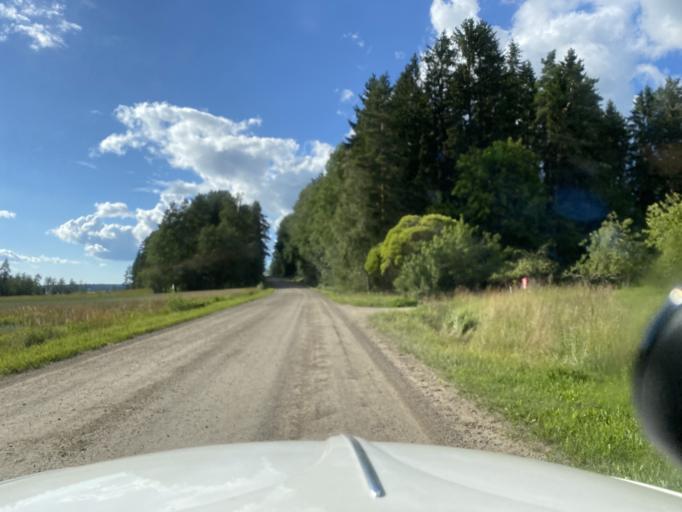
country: FI
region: Pirkanmaa
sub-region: Lounais-Pirkanmaa
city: Punkalaidun
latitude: 61.1385
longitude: 23.2162
